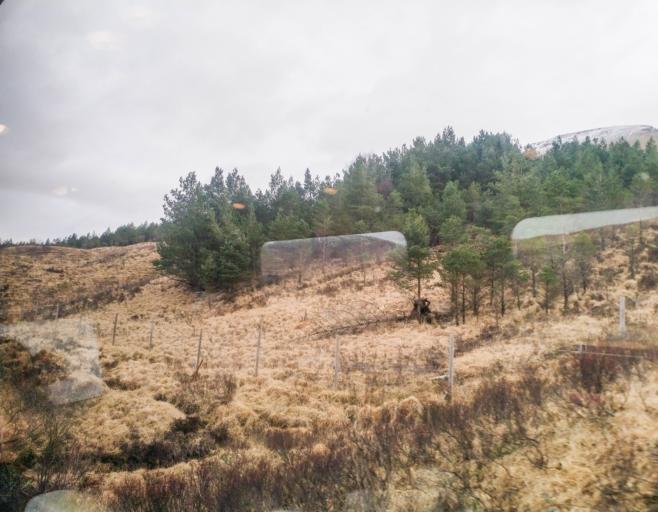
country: GB
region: Scotland
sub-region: Highland
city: Spean Bridge
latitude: 56.5233
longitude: -4.7635
